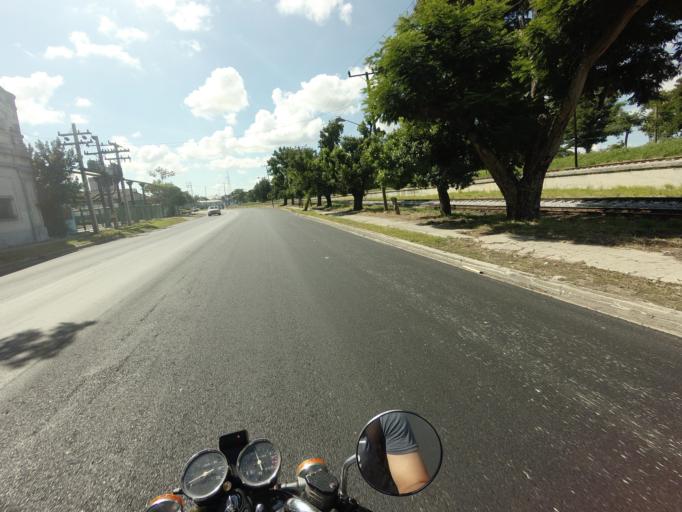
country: TM
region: Balkan
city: Gumdag
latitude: 38.8431
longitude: 54.1866
